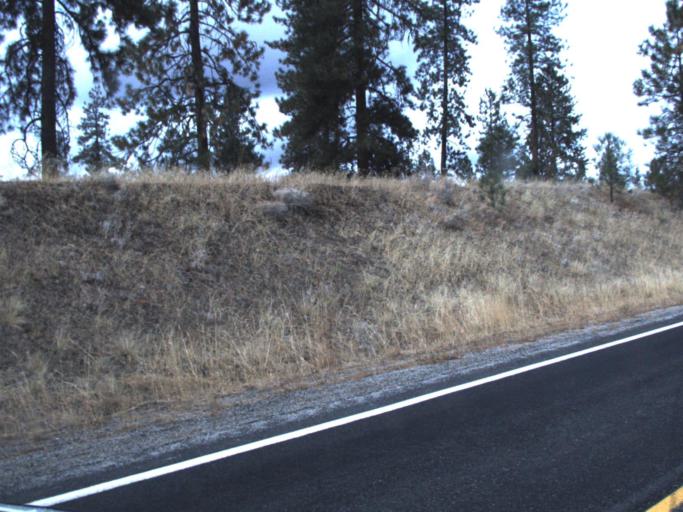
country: US
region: Washington
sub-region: Spokane County
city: Fairchild Air Force Base
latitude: 47.8802
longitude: -117.8395
